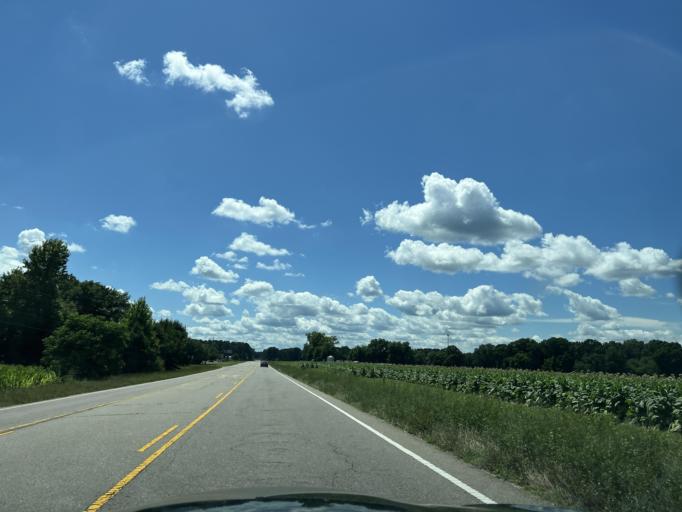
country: US
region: North Carolina
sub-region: Lee County
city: Sanford
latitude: 35.4376
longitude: -79.1963
